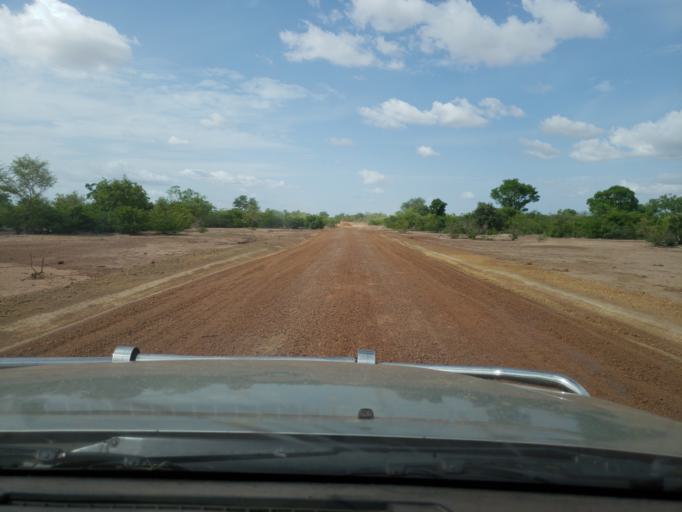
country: ML
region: Segou
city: Bla
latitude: 12.7754
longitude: -5.6120
